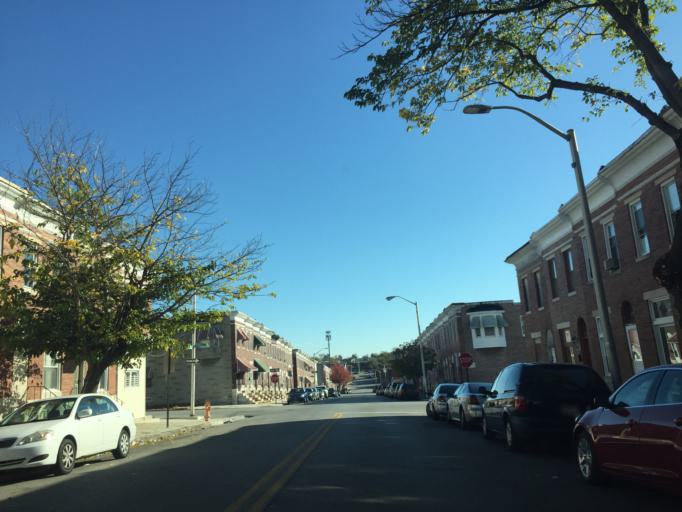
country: US
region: Maryland
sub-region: City of Baltimore
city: Baltimore
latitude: 39.3108
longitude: -76.5922
